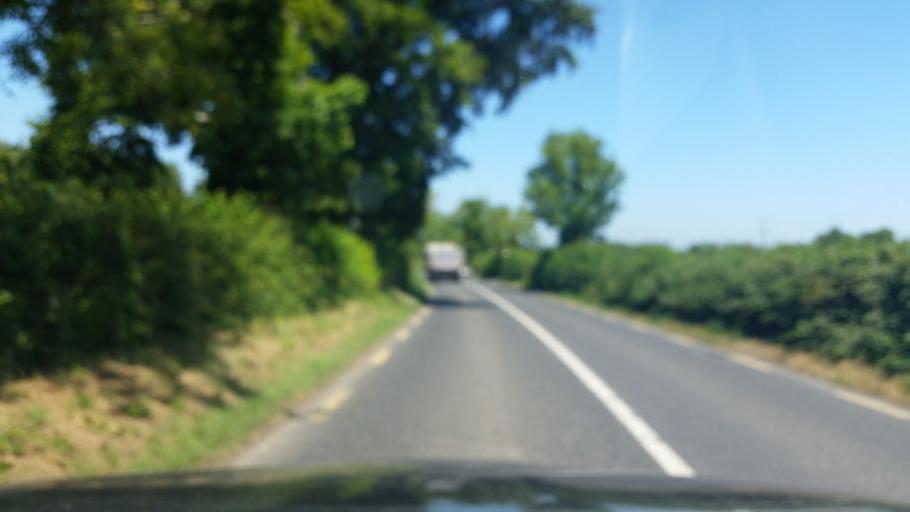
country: IE
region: Leinster
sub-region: Fingal County
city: Swords
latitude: 53.4819
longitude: -6.2707
